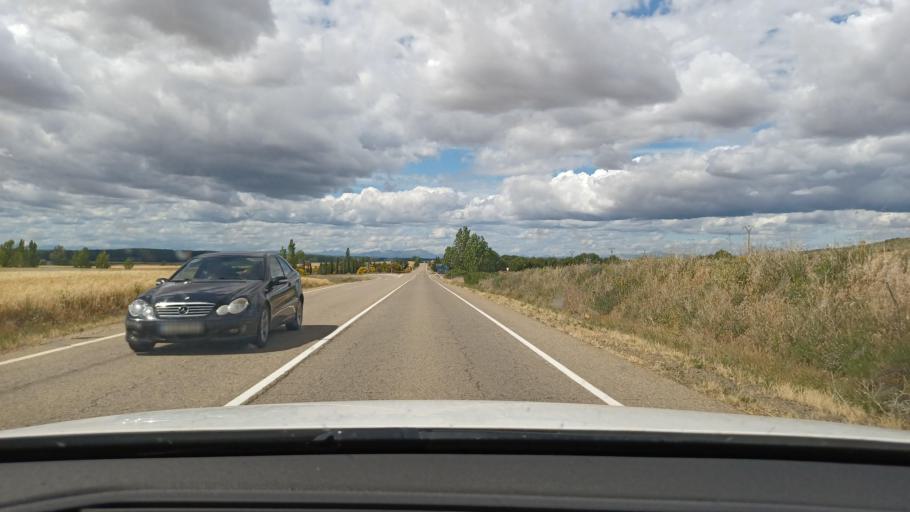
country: ES
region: Castille and Leon
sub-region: Provincia de Leon
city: Sahagun
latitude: 42.3814
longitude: -5.0274
